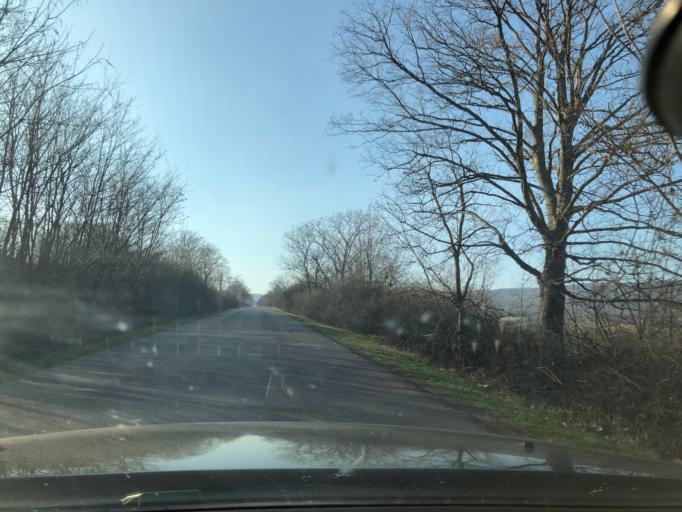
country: HU
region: Nograd
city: Paszto
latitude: 47.9089
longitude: 19.6612
